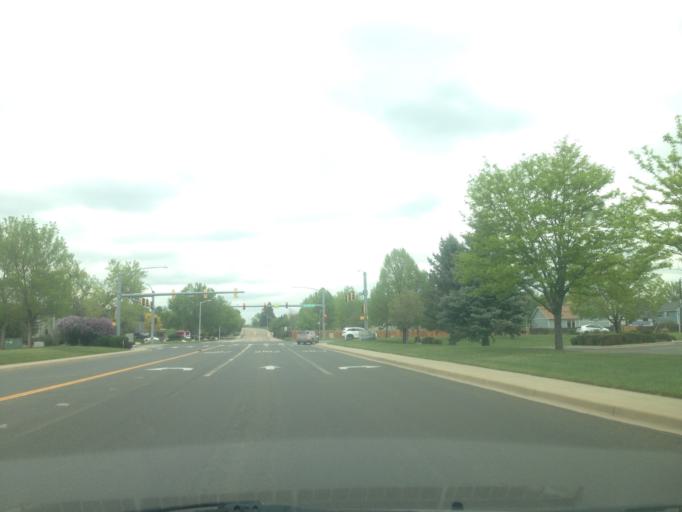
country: US
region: Colorado
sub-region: Boulder County
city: Longmont
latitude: 40.1369
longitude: -105.1215
